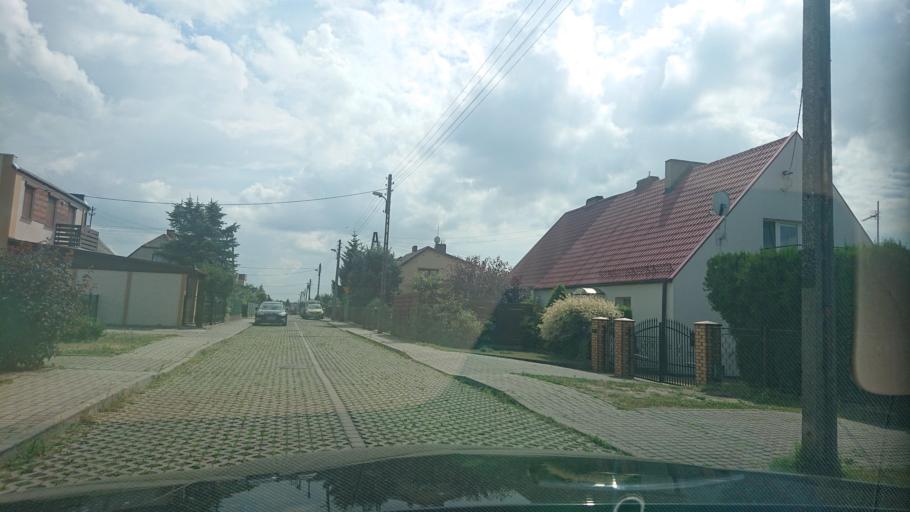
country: PL
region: Greater Poland Voivodeship
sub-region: Powiat gnieznienski
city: Gniezno
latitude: 52.5090
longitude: 17.5913
